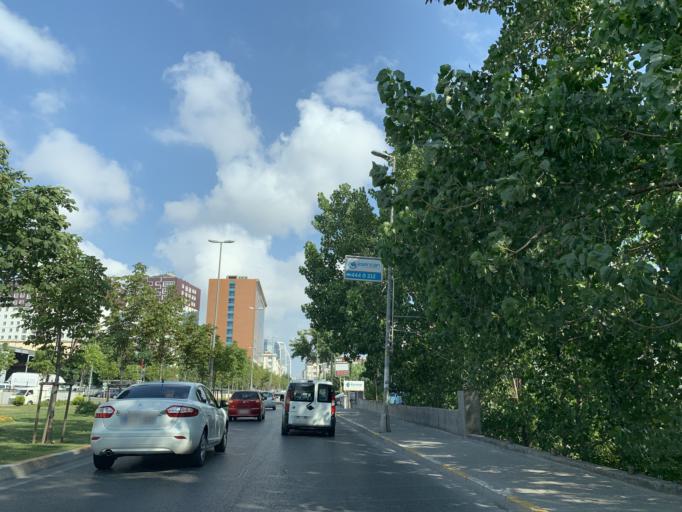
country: TR
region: Istanbul
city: Esenyurt
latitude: 41.0273
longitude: 28.6671
